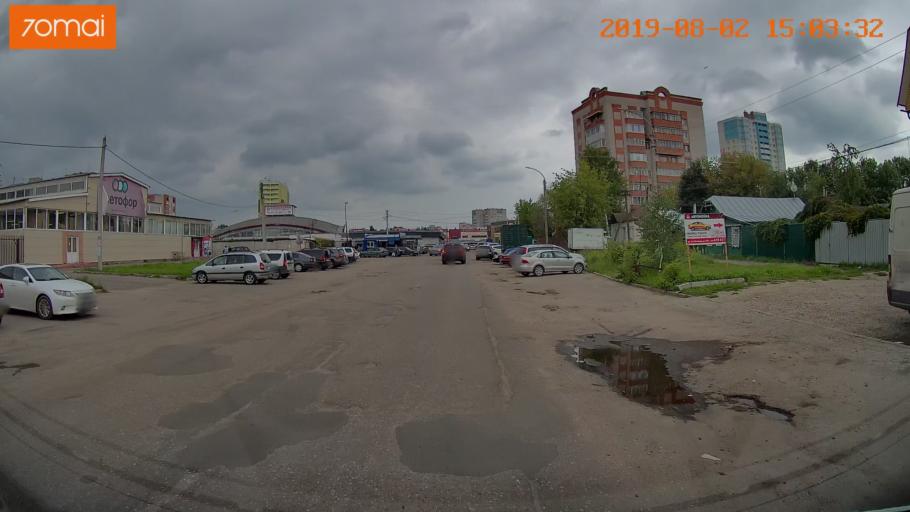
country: RU
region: Ivanovo
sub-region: Gorod Ivanovo
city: Ivanovo
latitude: 56.9902
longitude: 40.9657
